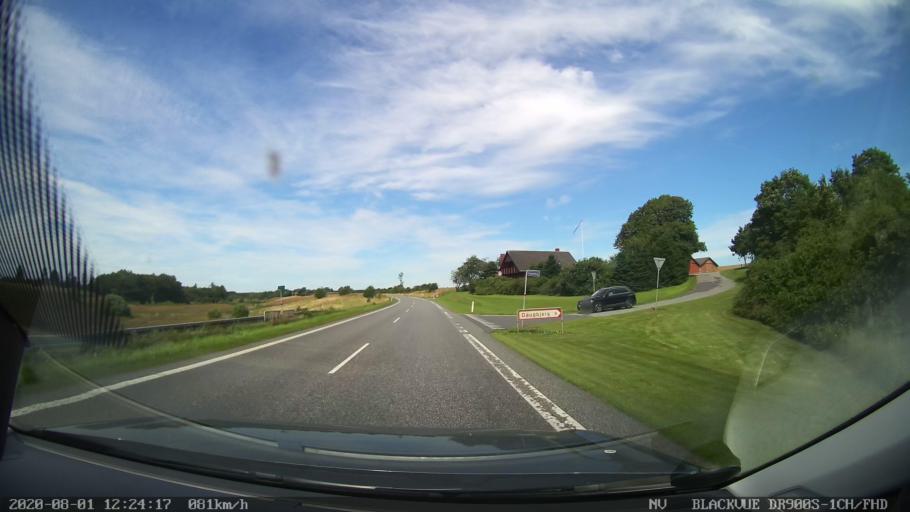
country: DK
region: Central Jutland
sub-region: Viborg Kommune
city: Stoholm
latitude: 56.4039
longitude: 9.1304
